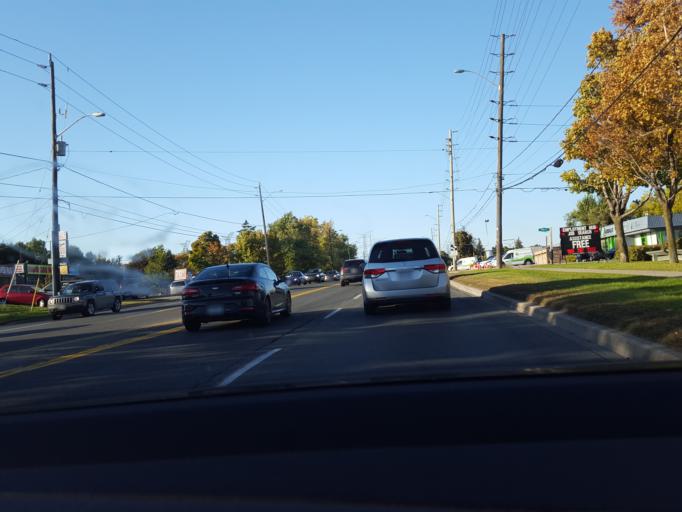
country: CA
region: Ontario
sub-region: York
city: Richmond Hill
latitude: 43.8275
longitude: -79.4270
